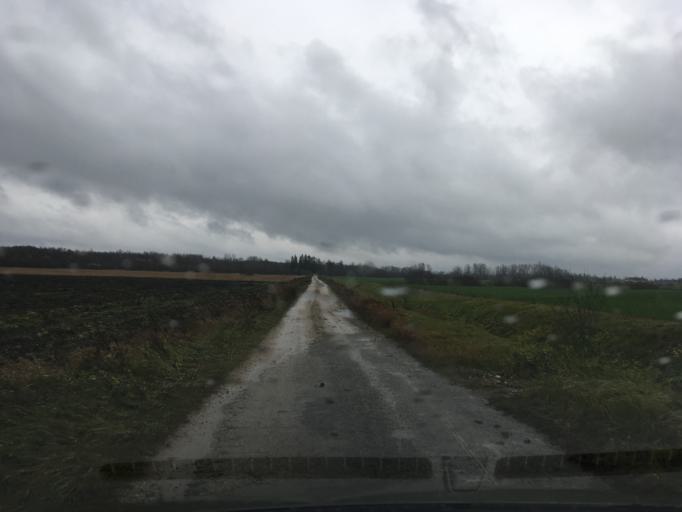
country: EE
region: Laeaene
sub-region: Lihula vald
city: Lihula
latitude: 58.7052
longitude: 23.8536
